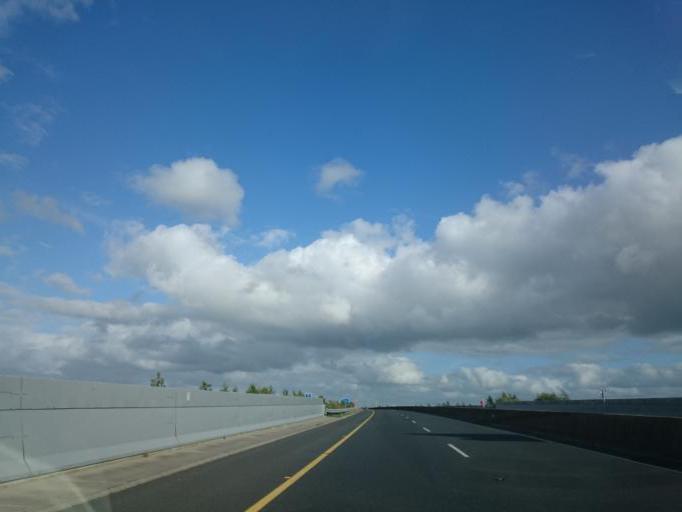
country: IE
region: Connaught
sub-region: County Galway
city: Athenry
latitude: 53.2835
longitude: -8.7521
